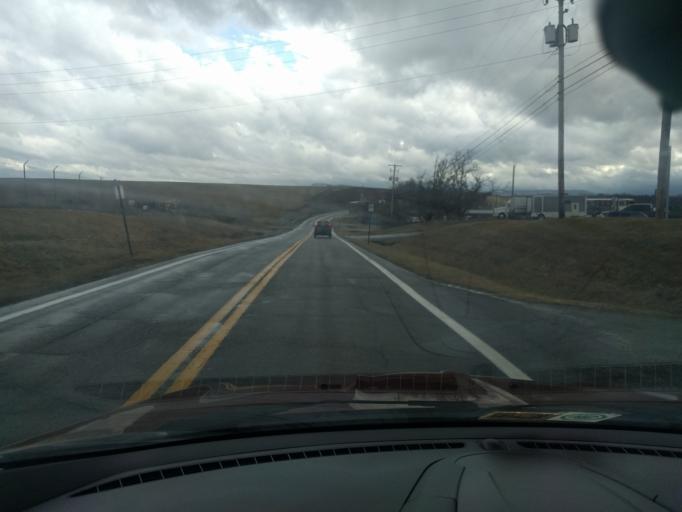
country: US
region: Virginia
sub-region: Roanoke County
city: Hollins
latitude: 37.3263
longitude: -79.9858
